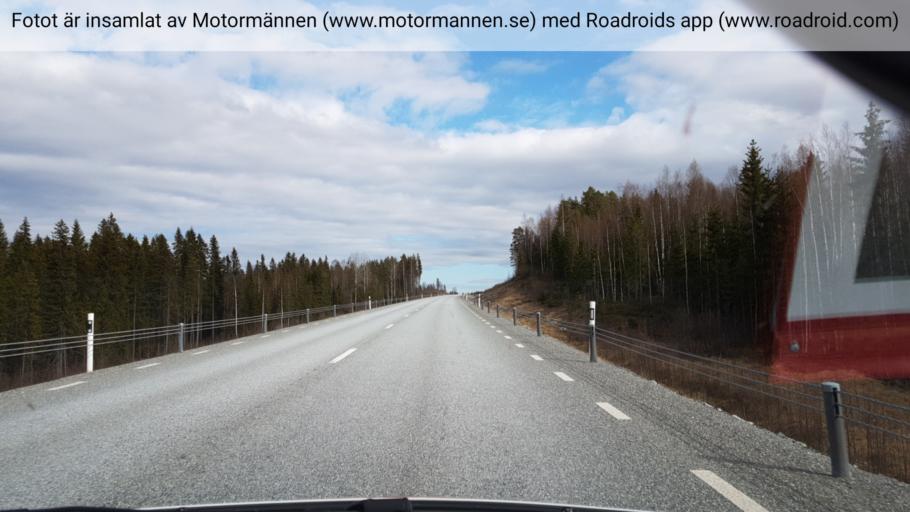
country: SE
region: Vaesternorrland
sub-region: Kramfors Kommun
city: Bollstabruk
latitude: 63.0674
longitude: 17.5818
